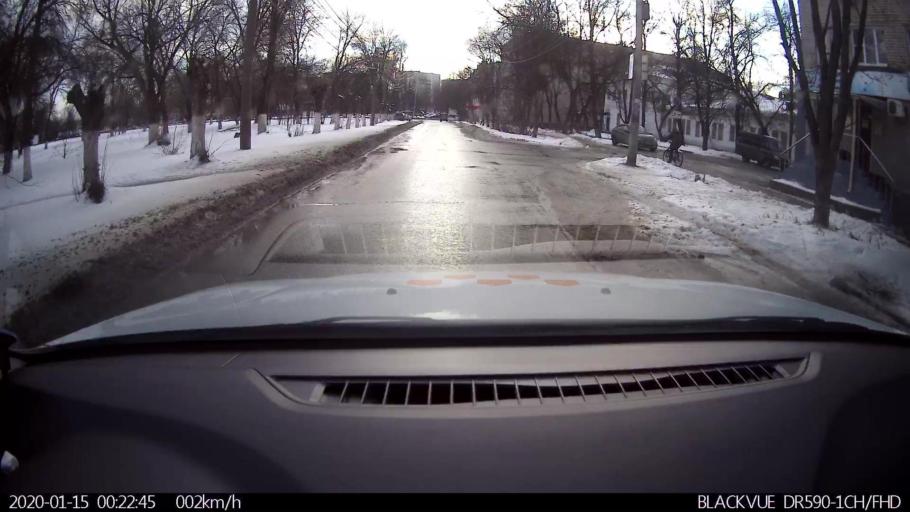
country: RU
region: Nizjnij Novgorod
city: Gorbatovka
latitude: 56.2460
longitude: 43.8681
